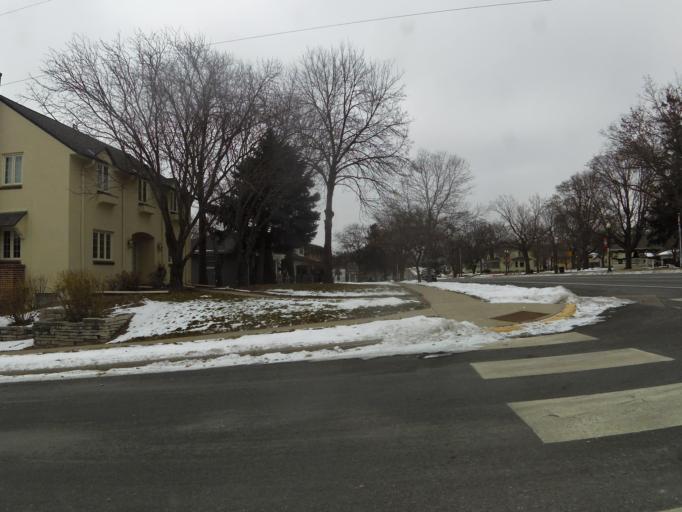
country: US
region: Minnesota
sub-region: Carver County
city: Waconia
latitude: 44.8505
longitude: -93.7845
